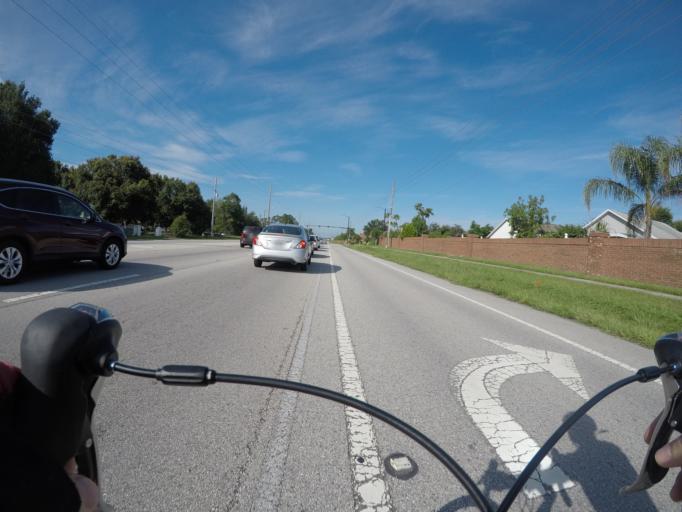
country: US
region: Florida
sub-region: Osceola County
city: Buenaventura Lakes
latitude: 28.3157
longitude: -81.3424
